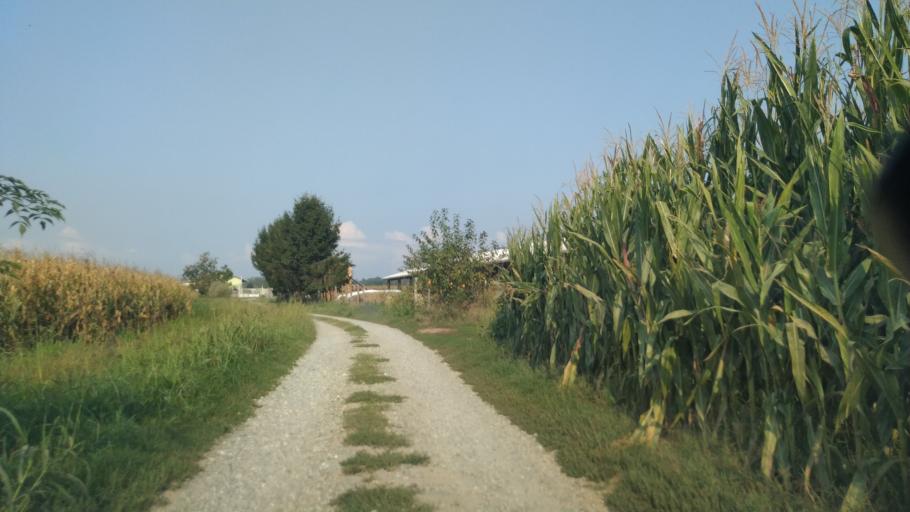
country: IT
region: Piedmont
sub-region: Provincia di Vercelli
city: Cigliano
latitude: 45.3256
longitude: 8.0302
